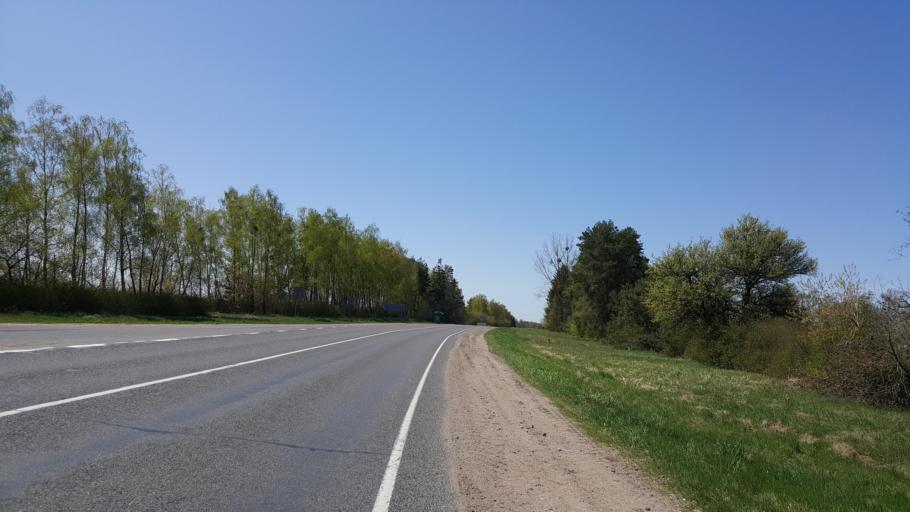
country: BY
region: Brest
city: Kamyanyets
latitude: 52.3692
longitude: 23.7911
